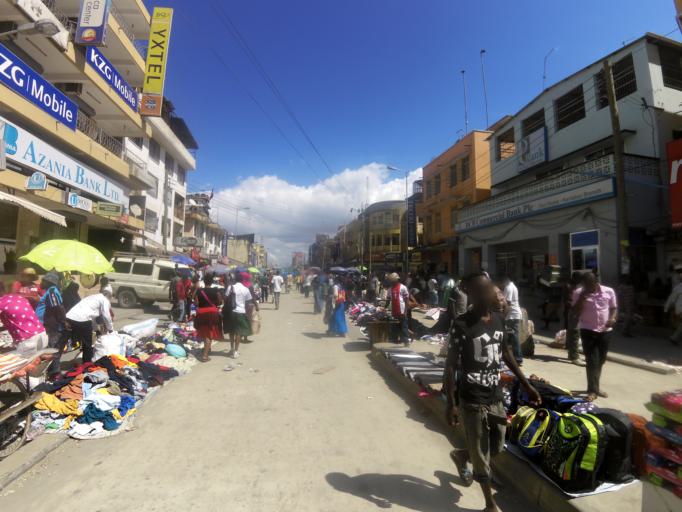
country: TZ
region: Dar es Salaam
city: Dar es Salaam
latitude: -6.8219
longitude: 39.2732
